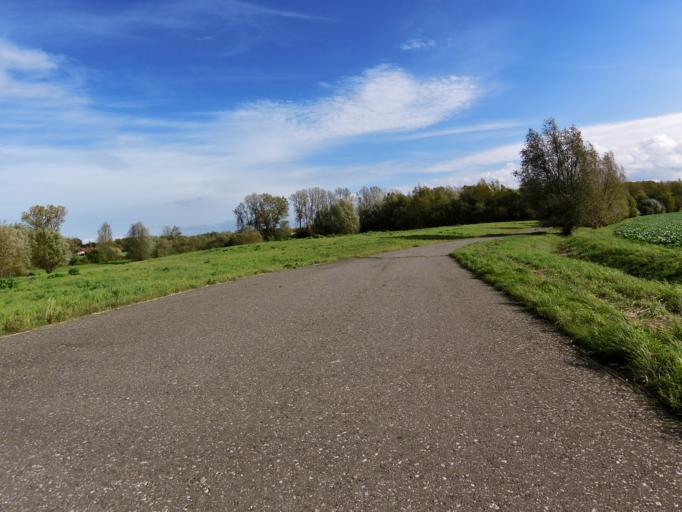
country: DE
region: Saxony
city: Grossposna
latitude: 51.3106
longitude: 12.4421
